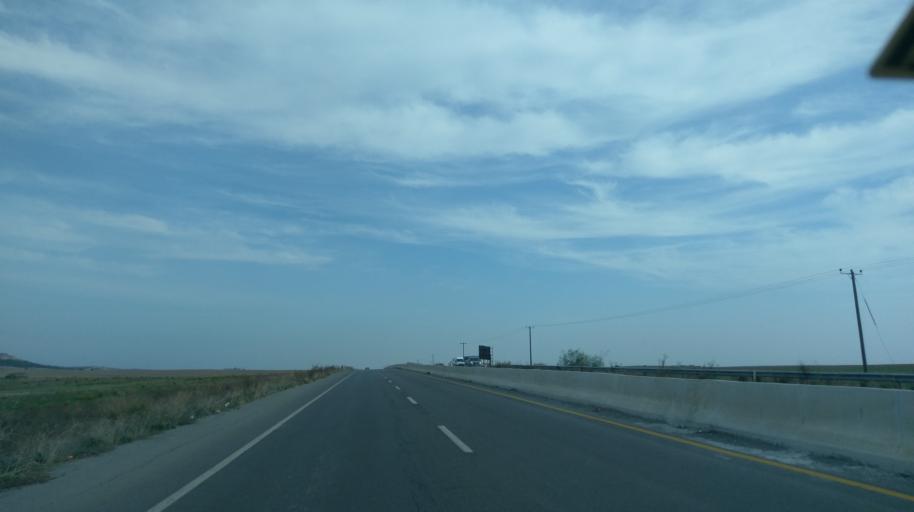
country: CY
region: Lefkosia
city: Mammari
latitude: 35.2137
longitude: 33.1929
